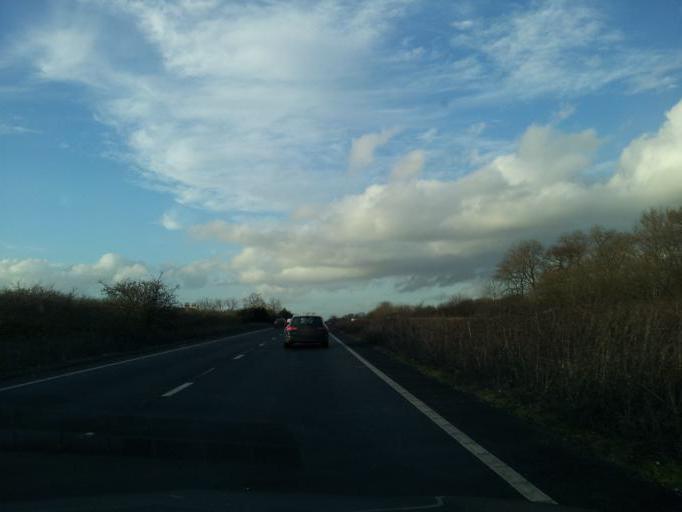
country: GB
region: England
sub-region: District of Rutland
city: Clipsham
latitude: 52.7209
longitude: -0.5955
